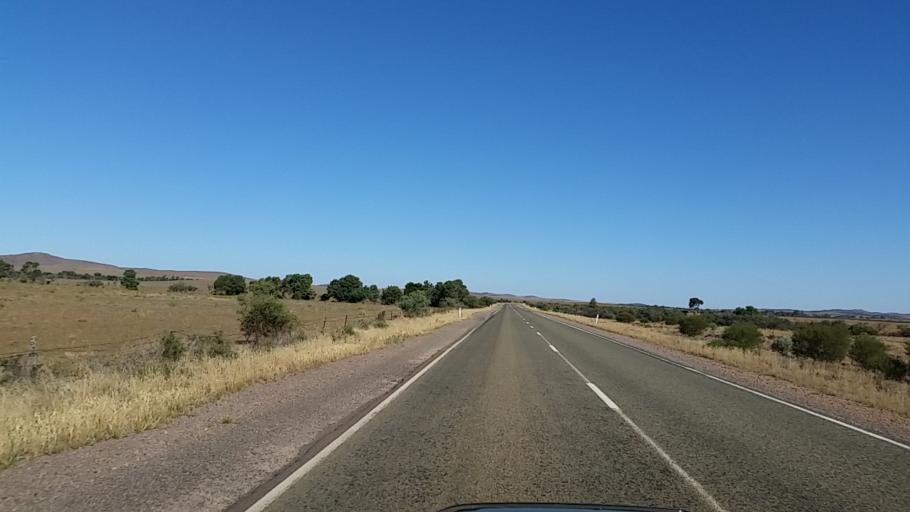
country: AU
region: South Australia
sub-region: Flinders Ranges
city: Quorn
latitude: -32.4337
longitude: 138.5332
